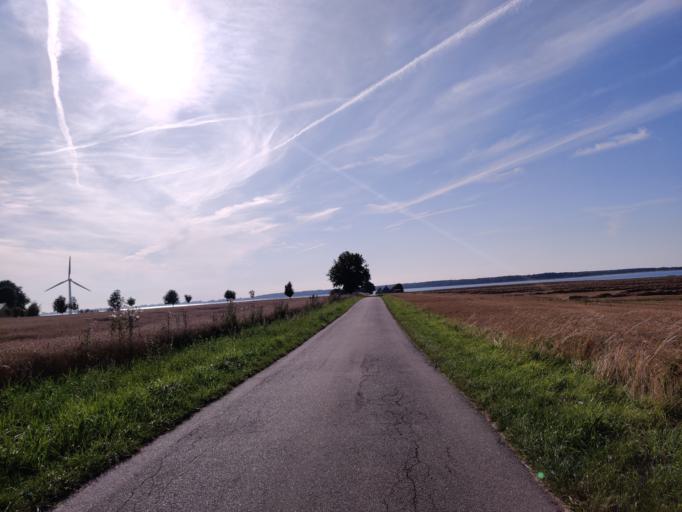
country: DK
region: Zealand
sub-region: Guldborgsund Kommune
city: Nykobing Falster
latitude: 54.6681
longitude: 11.8796
